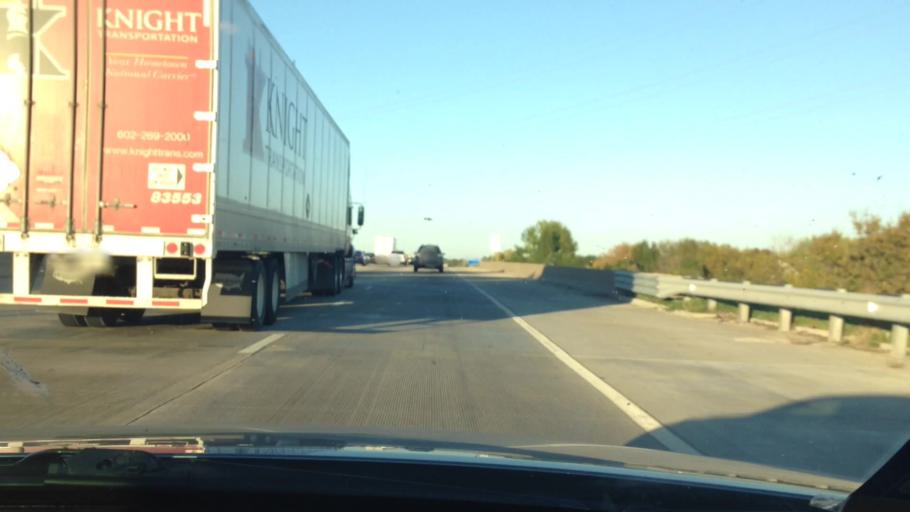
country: US
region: Kansas
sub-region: Johnson County
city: Olathe
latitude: 38.8617
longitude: -94.8074
